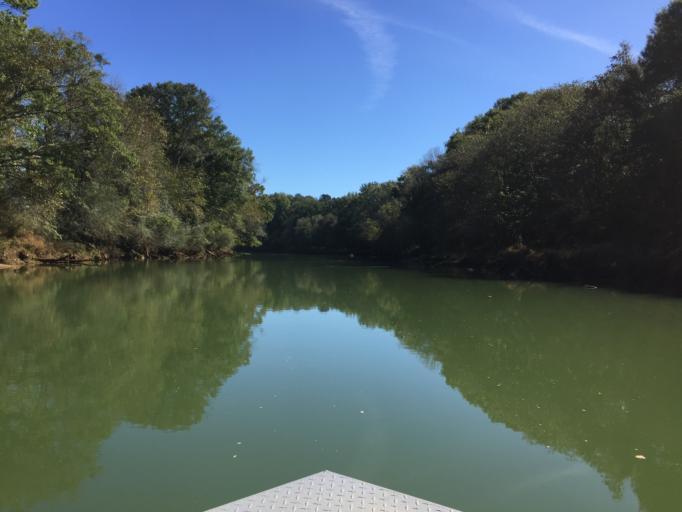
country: US
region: Georgia
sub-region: Gwinnett County
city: Duluth
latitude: 34.0333
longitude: -84.1266
